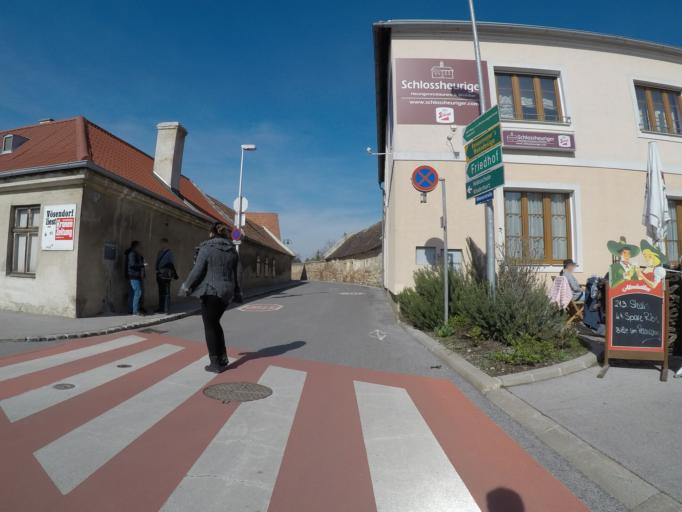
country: AT
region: Lower Austria
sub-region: Politischer Bezirk Modling
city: Vosendorf
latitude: 48.1212
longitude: 16.3409
